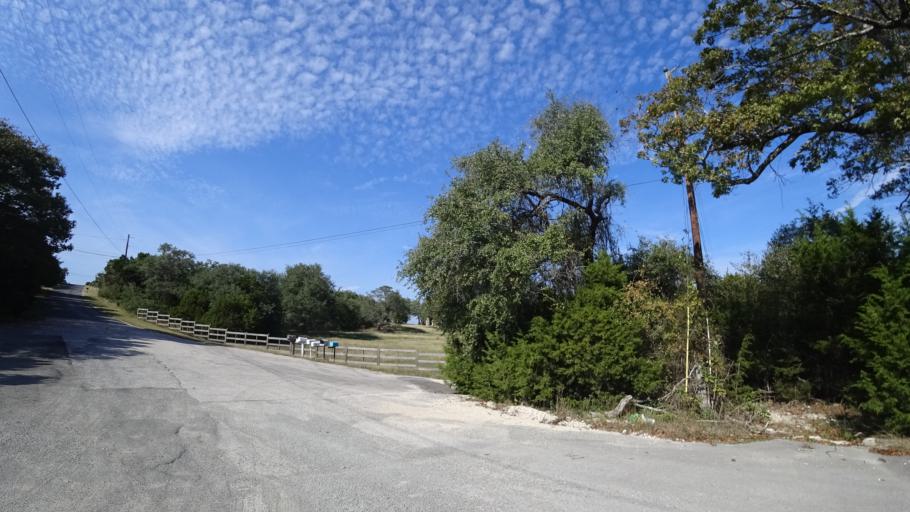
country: US
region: Texas
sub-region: Travis County
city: Shady Hollow
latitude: 30.2211
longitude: -97.9206
